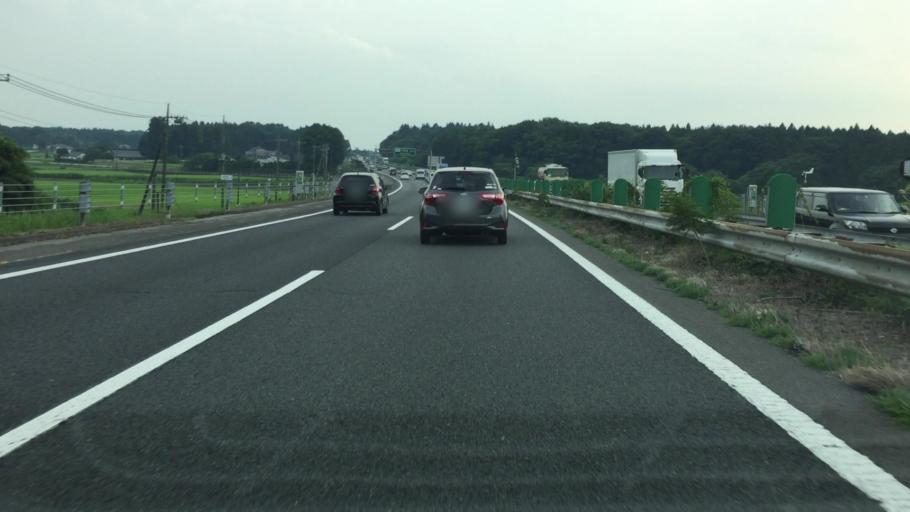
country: JP
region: Tochigi
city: Utsunomiya-shi
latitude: 36.6489
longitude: 139.8563
